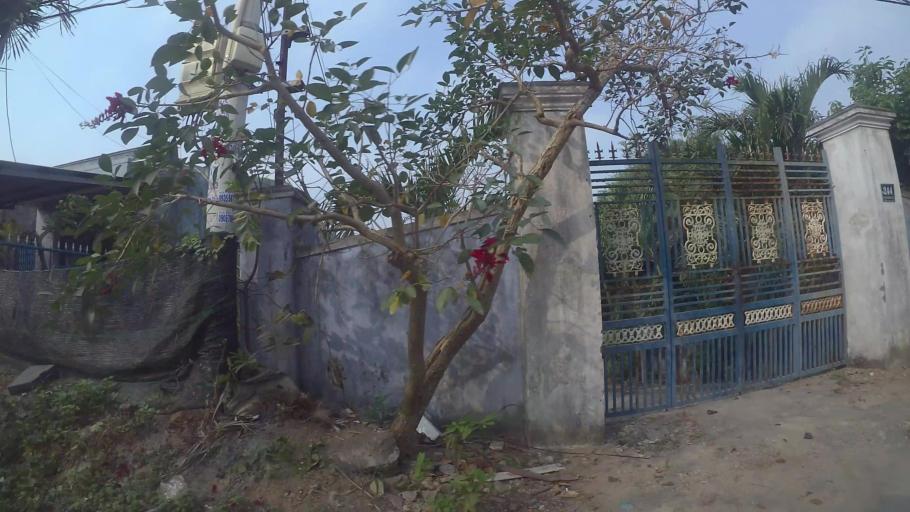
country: VN
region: Da Nang
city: Ngu Hanh Son
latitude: 16.0193
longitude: 108.2492
